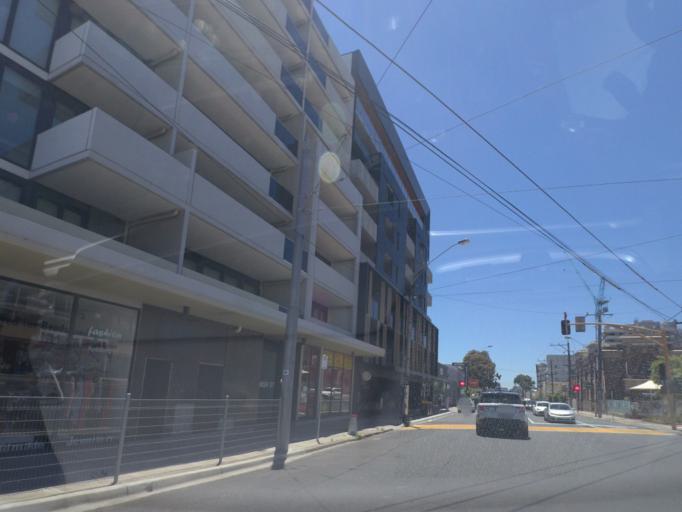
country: AU
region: Victoria
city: Thornbury
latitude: -37.7522
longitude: 145.0017
